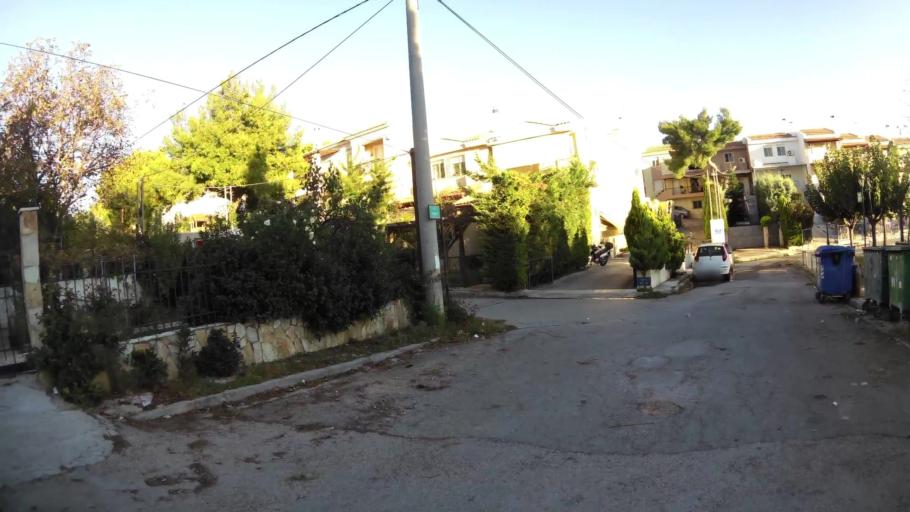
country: GR
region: Attica
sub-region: Nomarchia Anatolikis Attikis
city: Kryoneri
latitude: 38.1379
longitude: 23.8313
